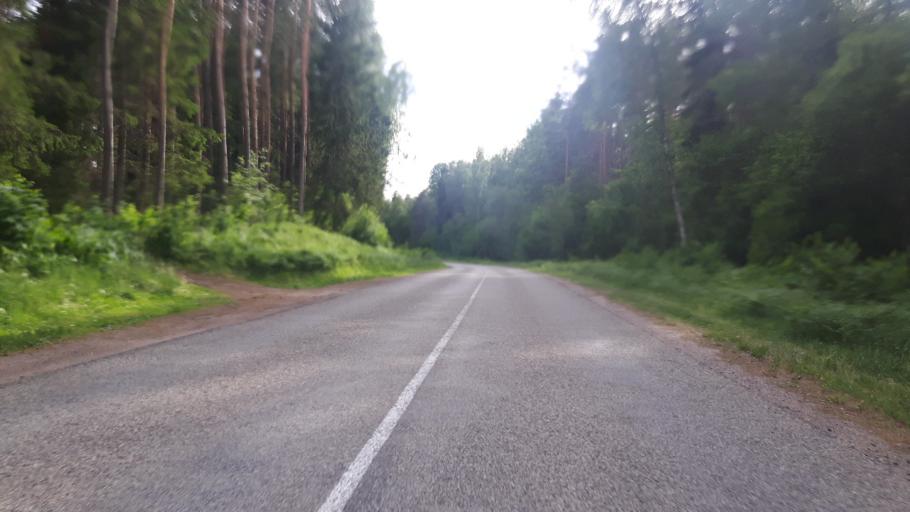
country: LV
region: Engure
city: Smarde
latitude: 56.9951
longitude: 23.3176
